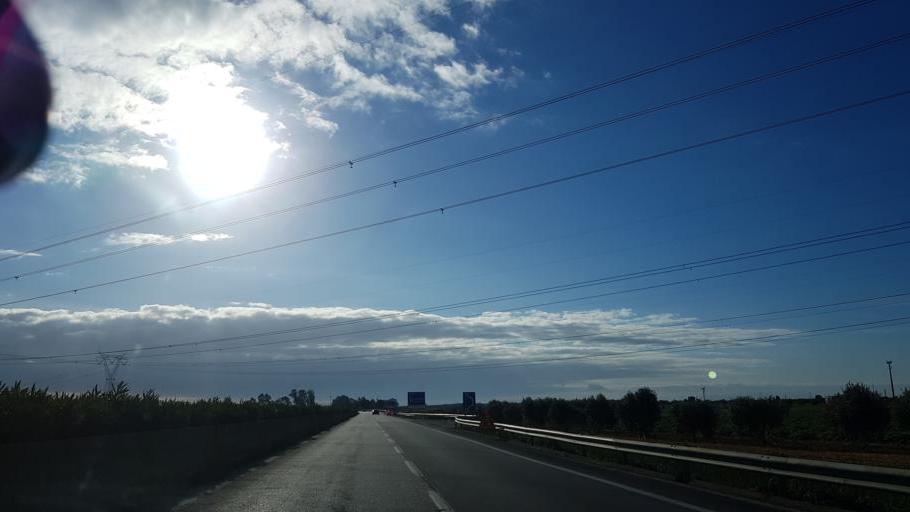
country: IT
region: Apulia
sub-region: Provincia di Brindisi
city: Tuturano
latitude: 40.5619
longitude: 17.9890
